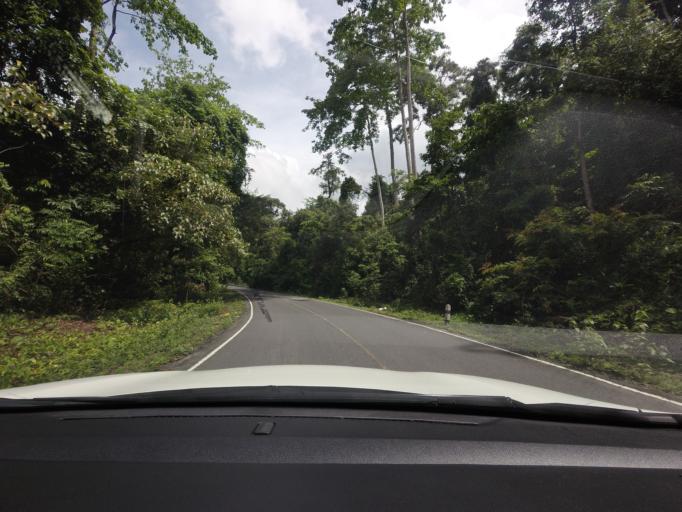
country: TH
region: Nakhon Nayok
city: Nakhon Nayok
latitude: 14.3410
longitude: 101.3498
